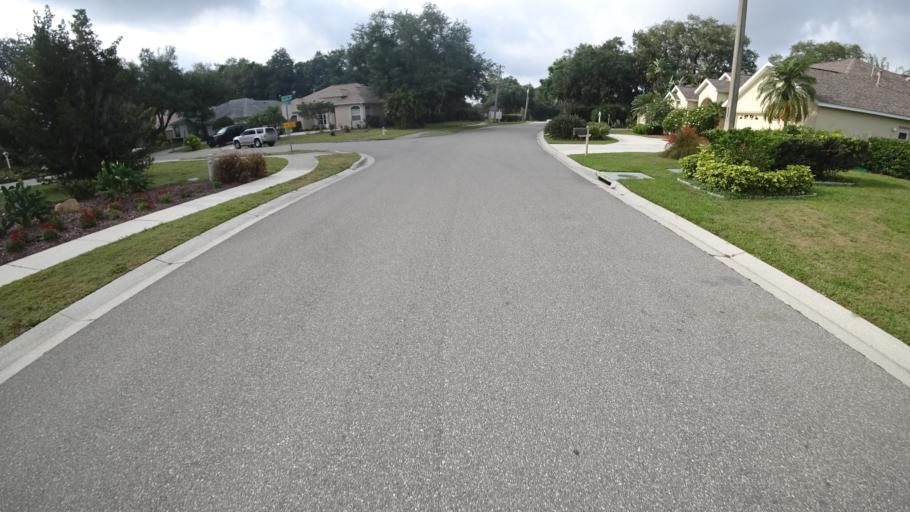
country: US
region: Florida
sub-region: Sarasota County
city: North Sarasota
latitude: 27.4077
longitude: -82.5095
